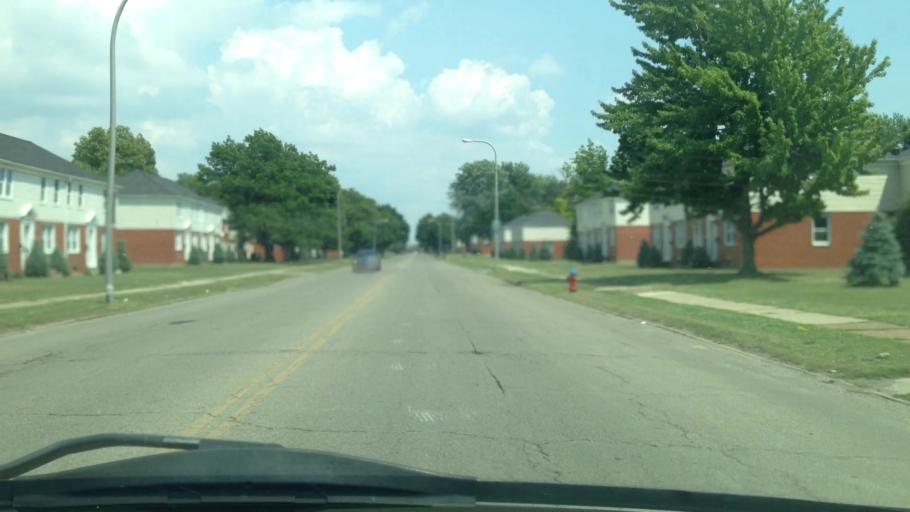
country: US
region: New York
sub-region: Erie County
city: Eggertsville
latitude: 42.9402
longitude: -78.8343
